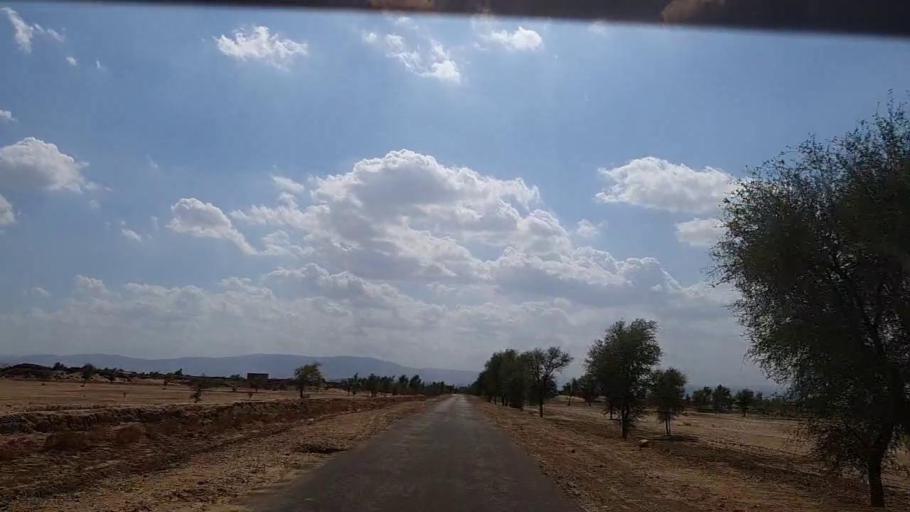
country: PK
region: Sindh
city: Johi
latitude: 26.5229
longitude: 67.4878
